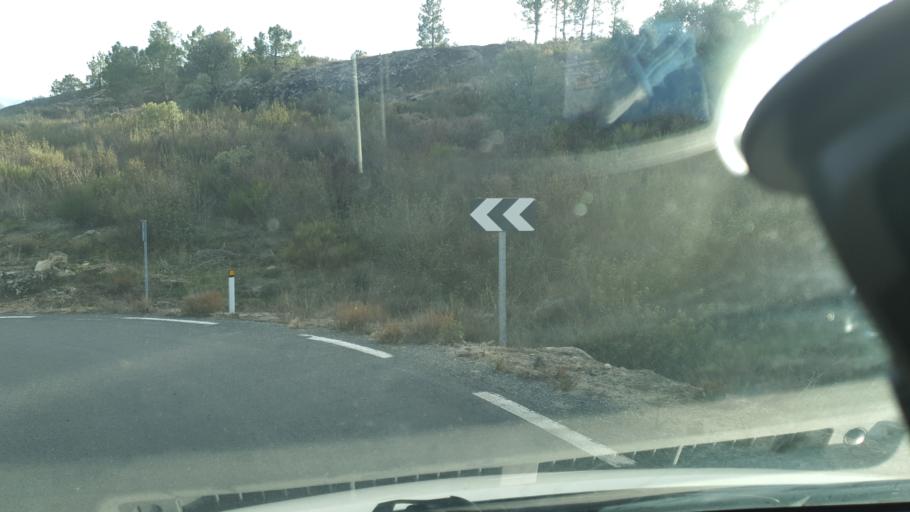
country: ES
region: Castille and Leon
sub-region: Provincia de Avila
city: Burgohondo
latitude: 40.4097
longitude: -4.8222
